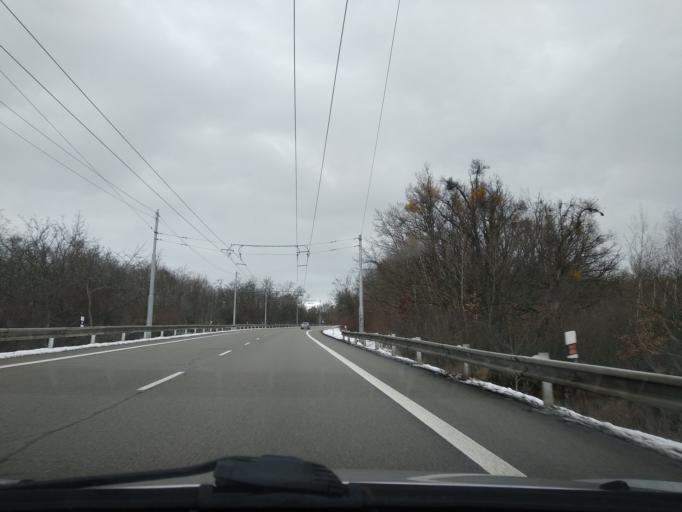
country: CZ
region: South Moravian
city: Ostopovice
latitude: 49.1798
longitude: 16.5449
